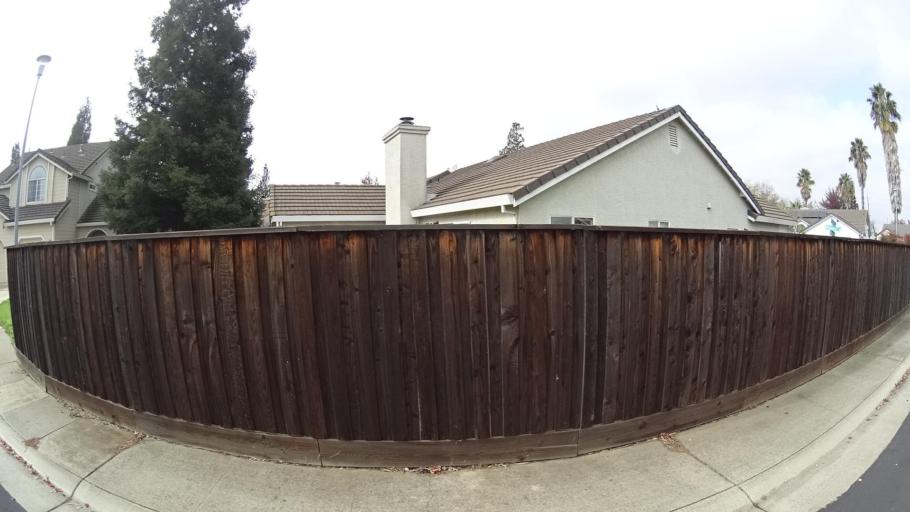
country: US
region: California
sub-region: Sacramento County
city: Elk Grove
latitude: 38.4222
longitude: -121.3562
